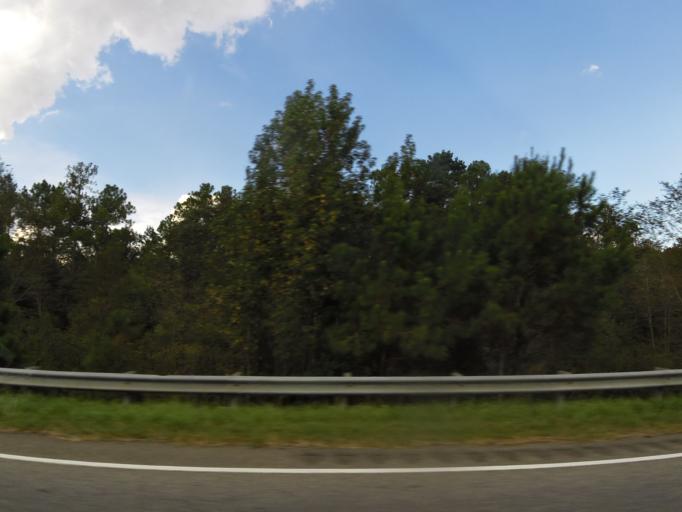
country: US
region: Georgia
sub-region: Brooks County
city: Quitman
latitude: 30.7866
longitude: -83.5189
